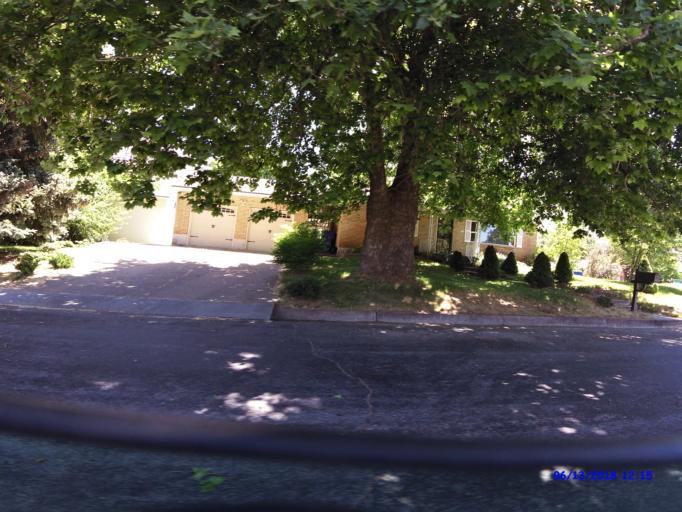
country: US
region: Utah
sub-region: Weber County
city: Ogden
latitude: 41.2122
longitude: -111.9384
